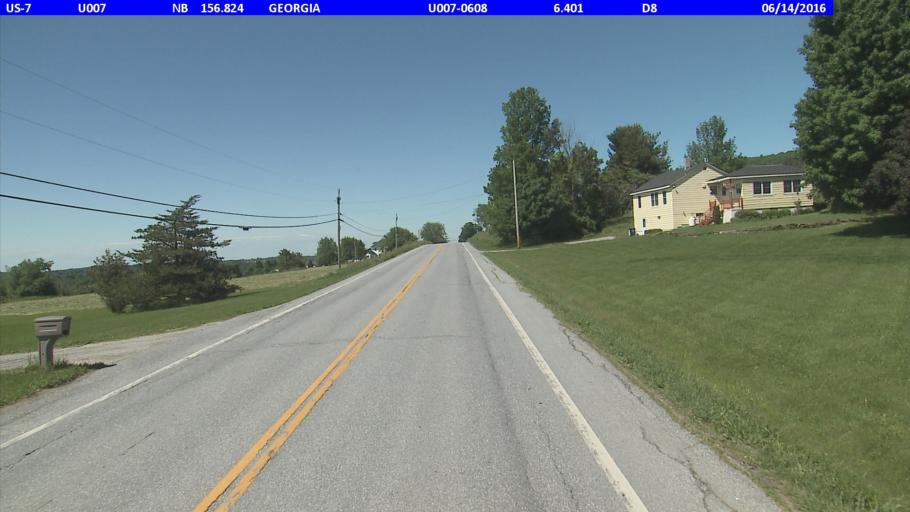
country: US
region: Vermont
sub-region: Franklin County
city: Saint Albans
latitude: 44.7632
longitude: -73.1093
